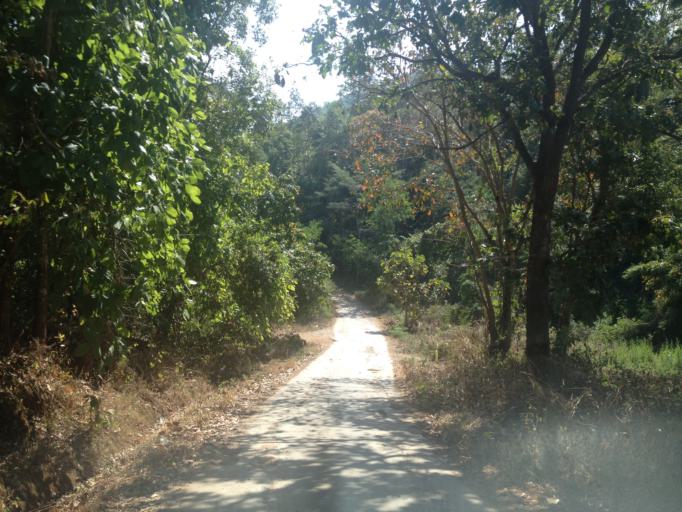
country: TH
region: Mae Hong Son
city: Ban Huai I Huak
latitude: 18.1067
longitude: 98.1895
